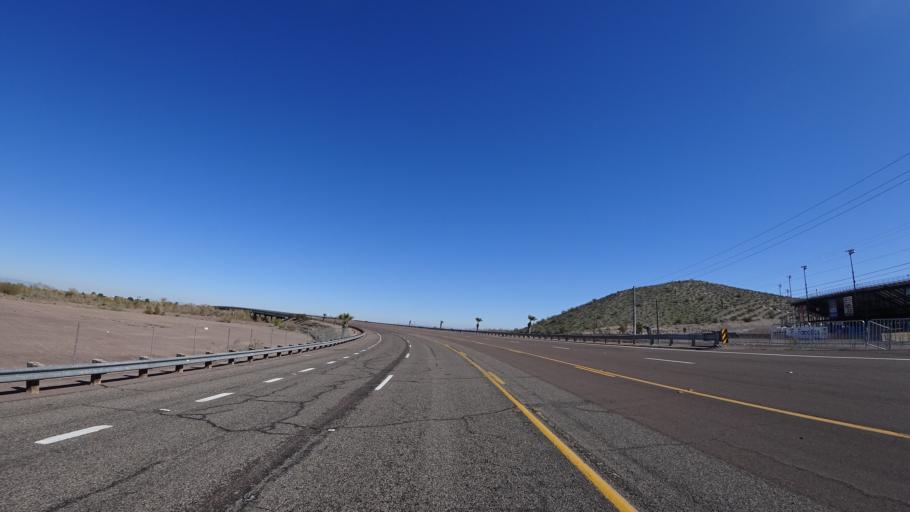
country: US
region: Arizona
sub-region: Maricopa County
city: Avondale
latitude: 33.3777
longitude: -112.3111
